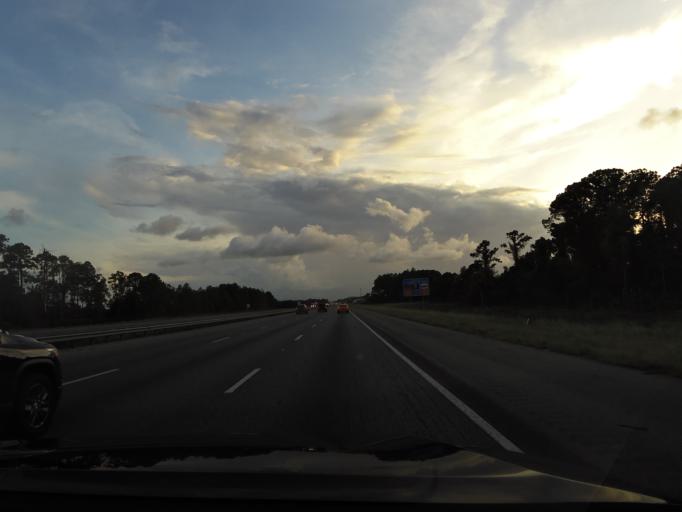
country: US
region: Georgia
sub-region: Glynn County
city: Dock Junction
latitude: 31.1615
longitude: -81.5579
